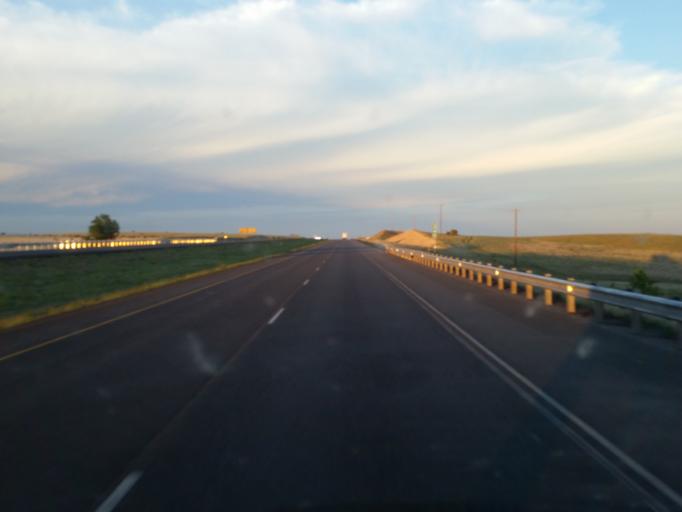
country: US
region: New Mexico
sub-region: Guadalupe County
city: Santa Rosa
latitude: 34.9906
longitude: -105.2780
